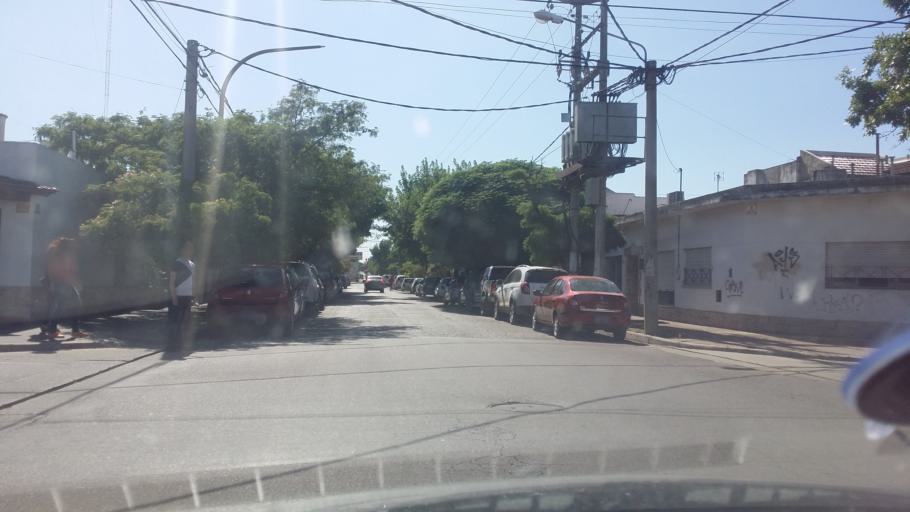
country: AR
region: La Pampa
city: Santa Rosa
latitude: -36.6220
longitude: -64.2835
